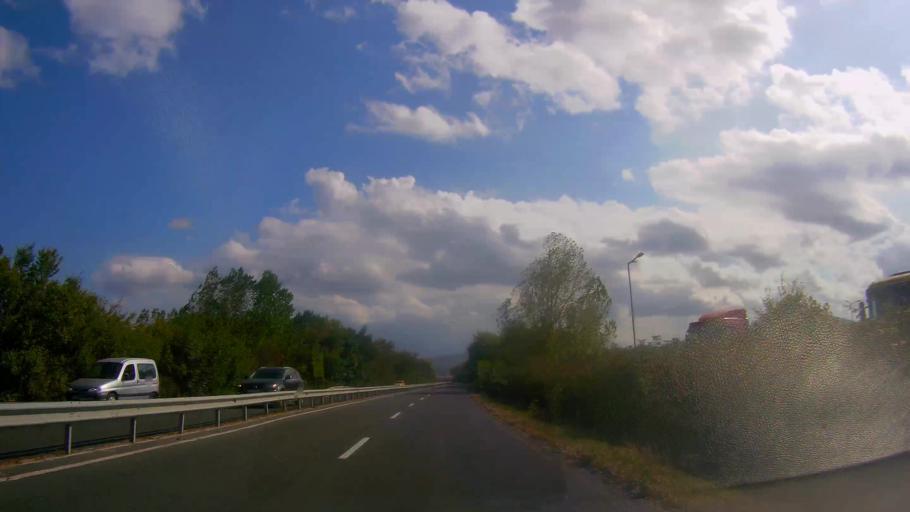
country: BG
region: Burgas
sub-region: Obshtina Sozopol
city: Chernomorets
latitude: 42.4370
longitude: 27.6370
